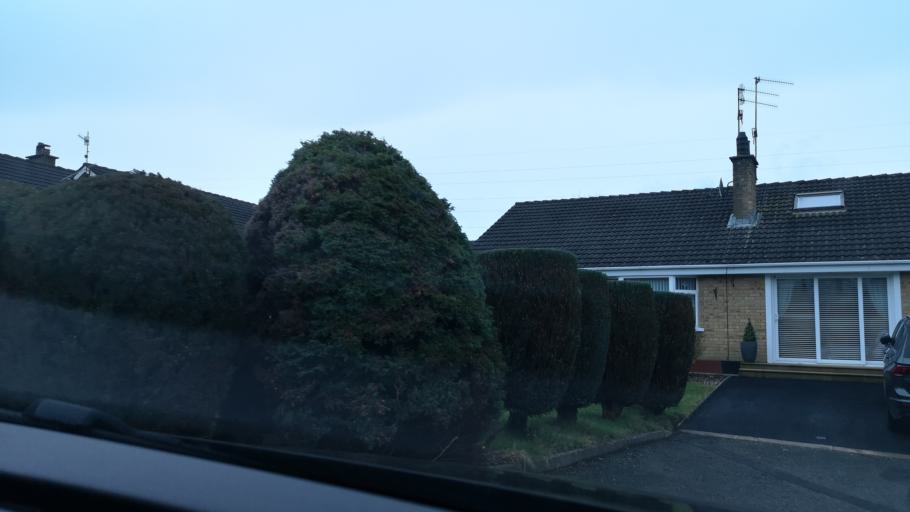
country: GB
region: Northern Ireland
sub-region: Newry and Mourne District
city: Newry
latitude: 54.1917
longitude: -6.3217
